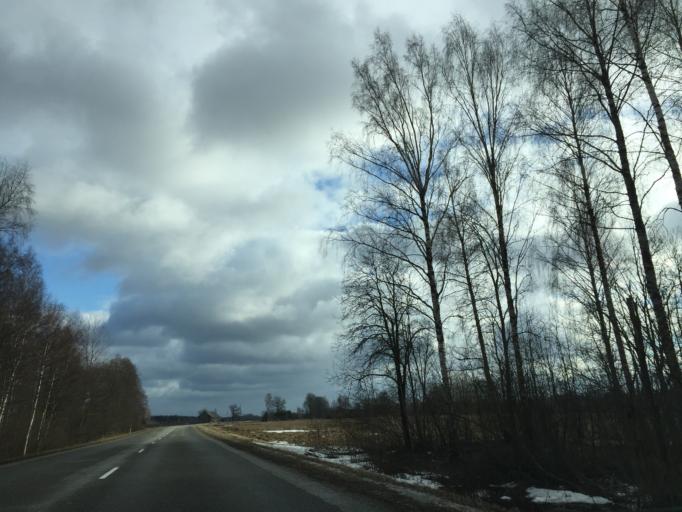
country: LV
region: Aloja
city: Staicele
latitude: 57.8749
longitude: 24.6751
